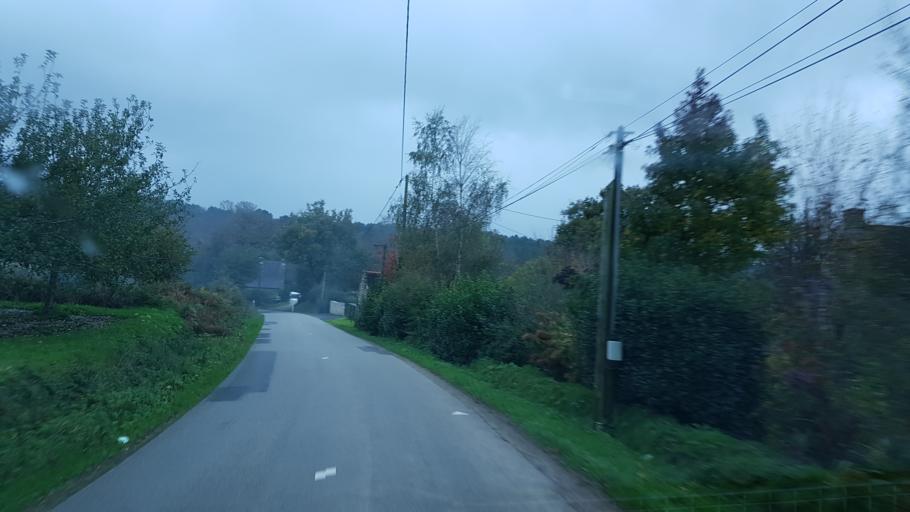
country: FR
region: Brittany
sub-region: Departement du Morbihan
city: Sulniac
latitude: 47.6978
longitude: -2.5872
